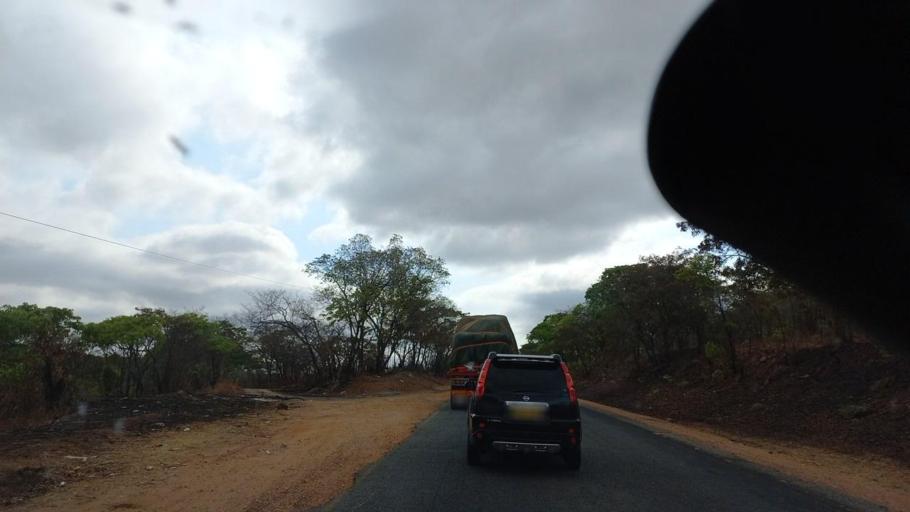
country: ZM
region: Lusaka
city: Chongwe
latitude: -15.1499
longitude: 29.3625
